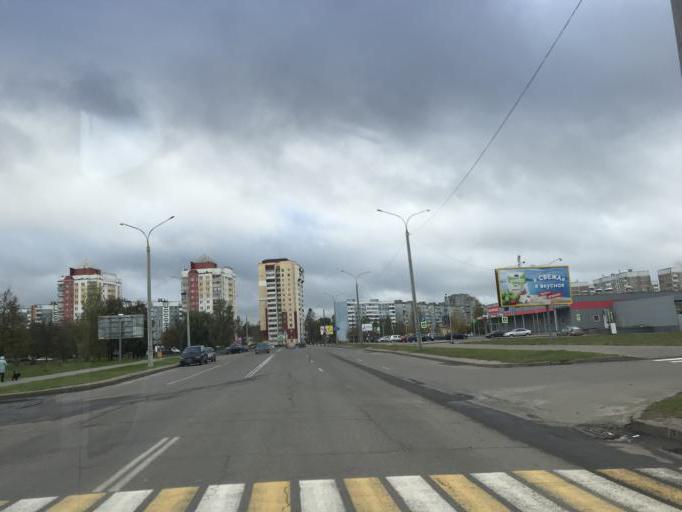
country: BY
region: Mogilev
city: Mahilyow
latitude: 53.8815
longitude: 30.3685
